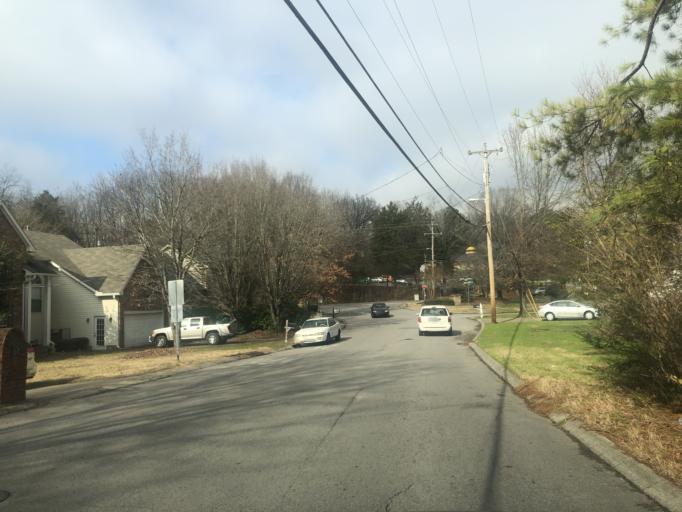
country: US
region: Tennessee
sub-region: Rutherford County
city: La Vergne
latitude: 36.0772
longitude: -86.6565
